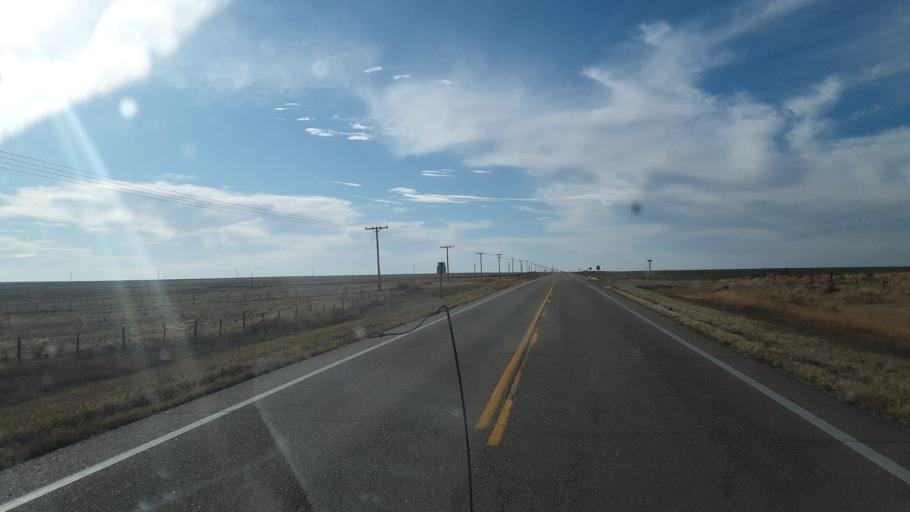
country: US
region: Kansas
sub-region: Finney County
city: Garden City
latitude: 38.0600
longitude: -100.6083
